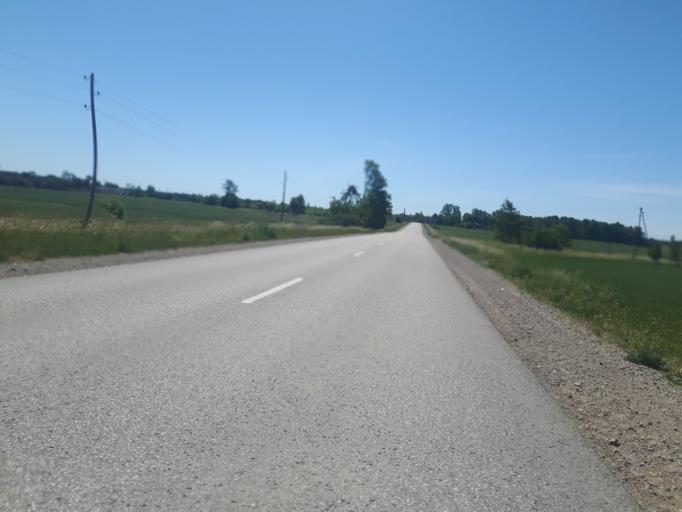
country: LV
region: Durbe
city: Liegi
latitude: 56.5714
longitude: 21.2708
